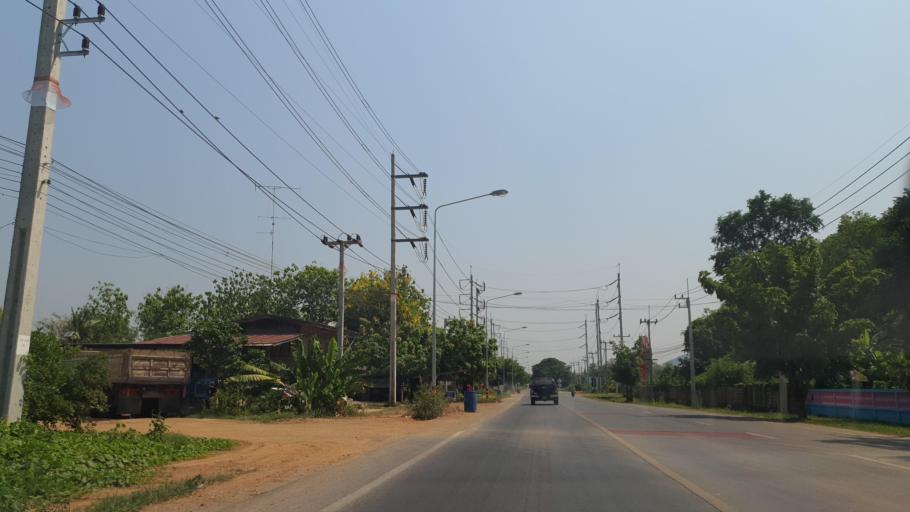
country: TH
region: Kanchanaburi
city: Kanchanaburi
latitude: 14.0550
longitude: 99.4748
